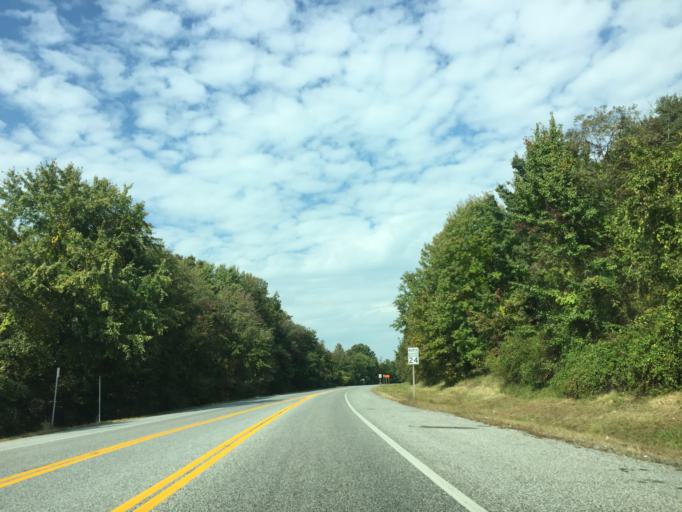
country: US
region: Maryland
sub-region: Harford County
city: Edgewood
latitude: 39.4179
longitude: -76.3080
